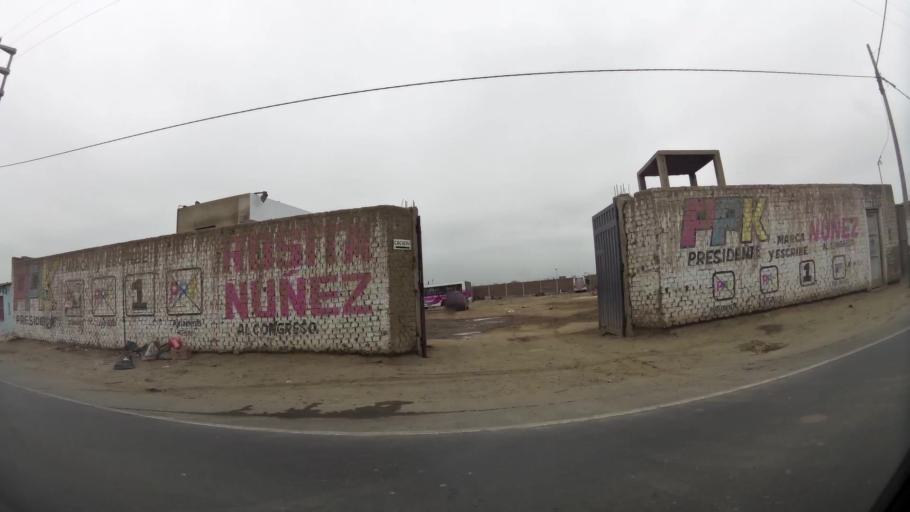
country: PE
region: La Libertad
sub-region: Provincia de Trujillo
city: Buenos Aires
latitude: -8.1374
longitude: -79.0574
